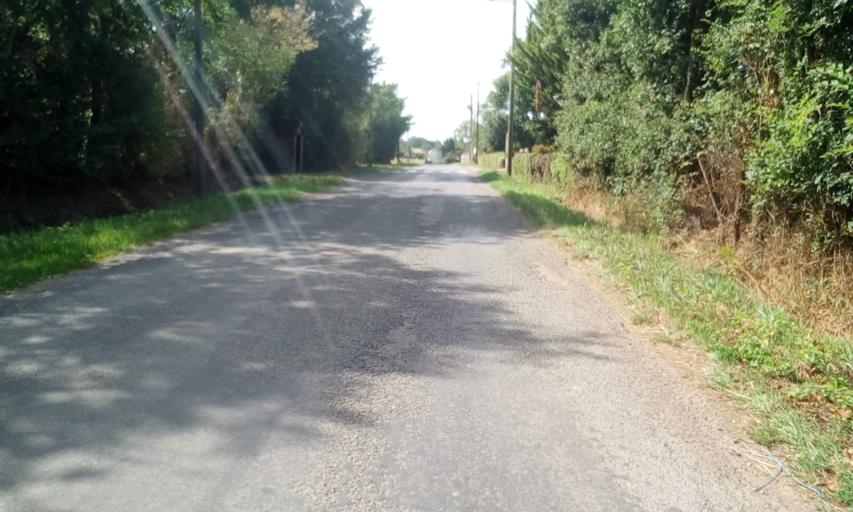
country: FR
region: Lower Normandy
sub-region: Departement du Calvados
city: Argences
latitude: 49.1542
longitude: -0.1476
